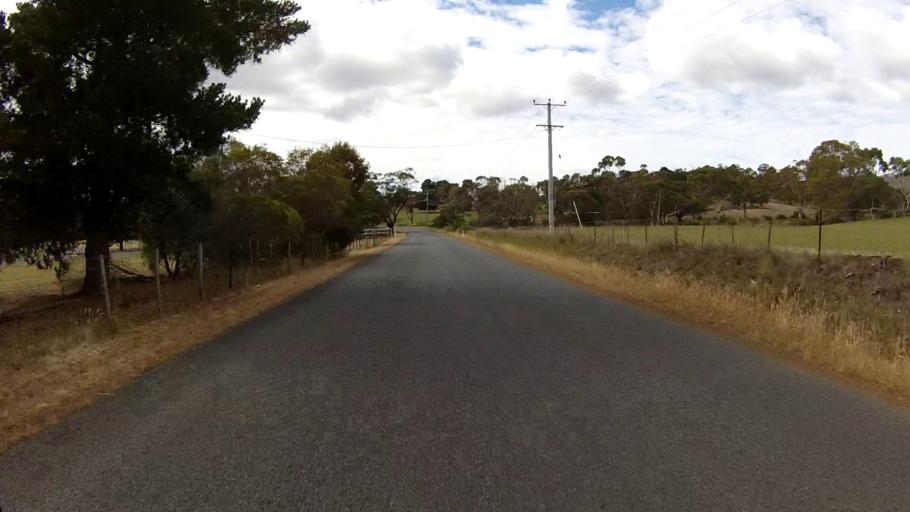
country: AU
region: Tasmania
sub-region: Clarence
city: Cambridge
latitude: -42.7705
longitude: 147.4102
